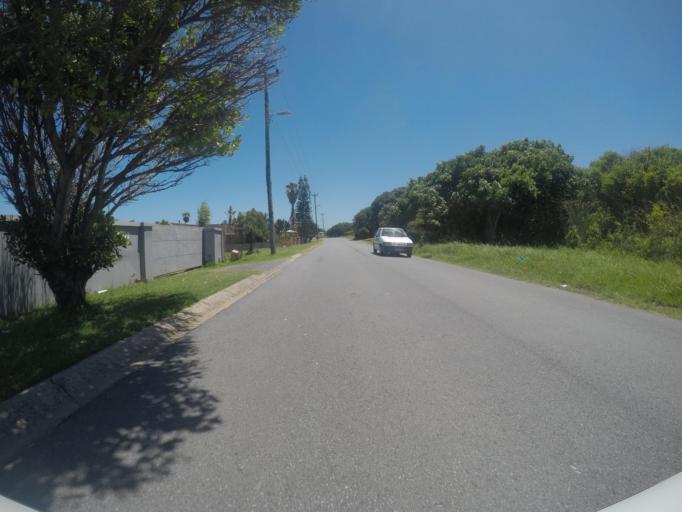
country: ZA
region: Eastern Cape
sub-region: Buffalo City Metropolitan Municipality
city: East London
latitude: -32.9527
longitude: 28.0080
